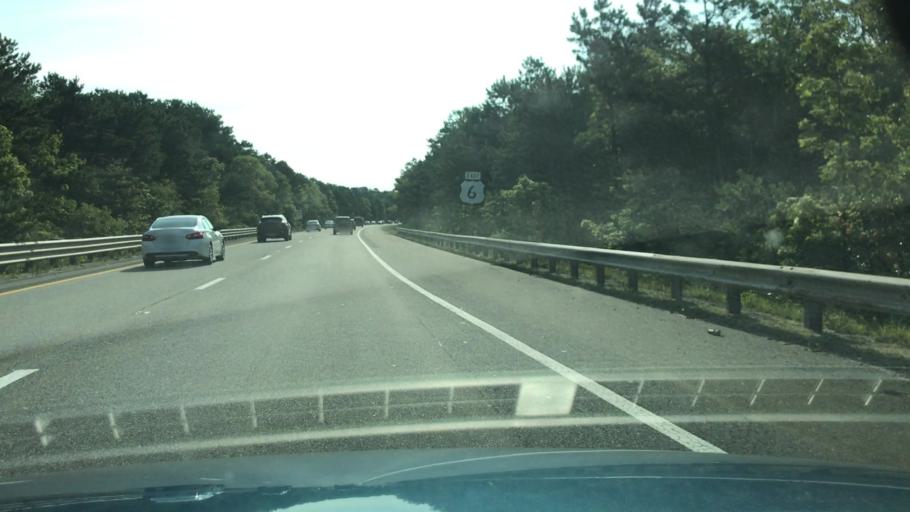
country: US
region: Massachusetts
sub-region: Barnstable County
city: Barnstable
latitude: 41.6888
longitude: -70.3303
